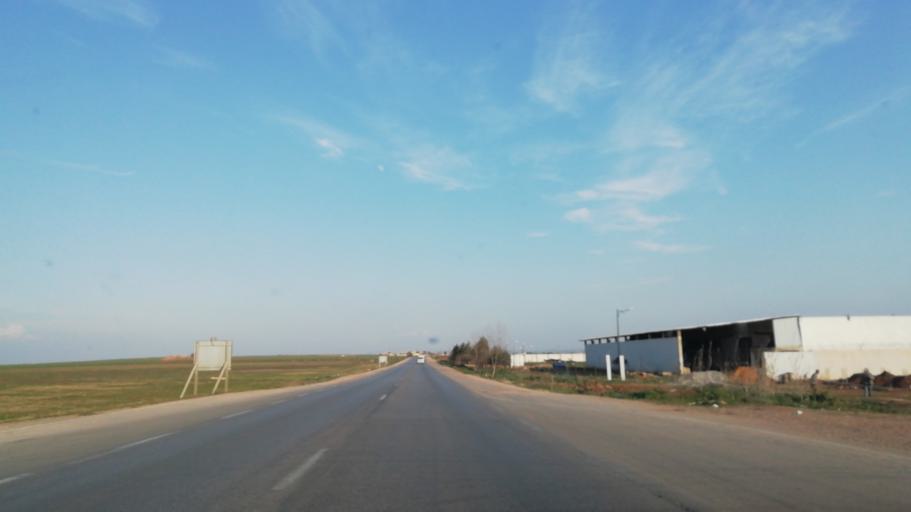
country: DZ
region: Relizane
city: Relizane
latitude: 35.8937
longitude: 0.6444
